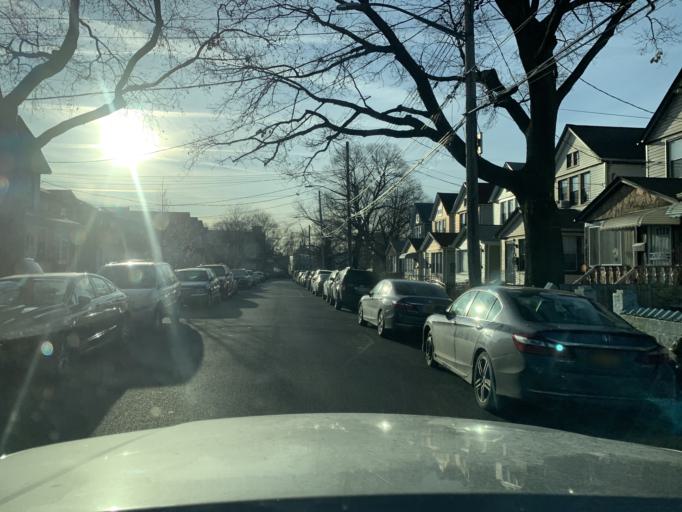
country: US
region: New York
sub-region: Queens County
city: Jamaica
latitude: 40.6924
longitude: -73.7894
